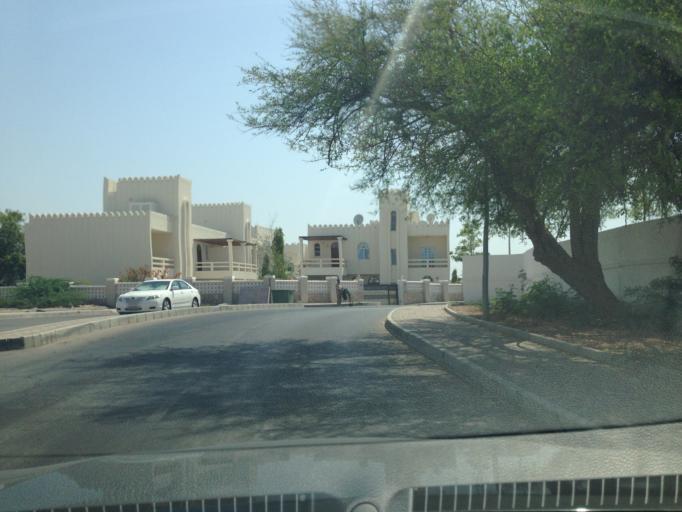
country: OM
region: Muhafazat Masqat
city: Muscat
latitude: 23.6304
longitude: 58.4864
